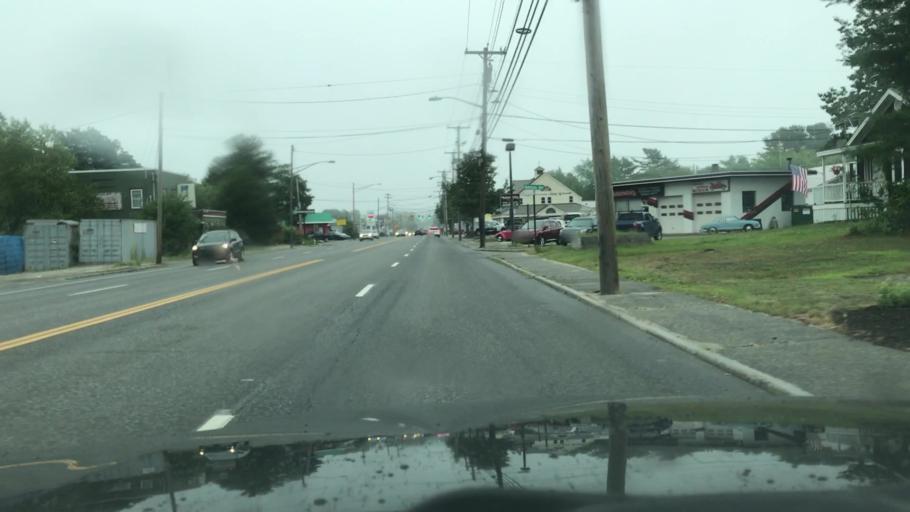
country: US
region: Maine
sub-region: Sagadahoc County
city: Topsham
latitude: 43.9121
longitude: -69.9909
